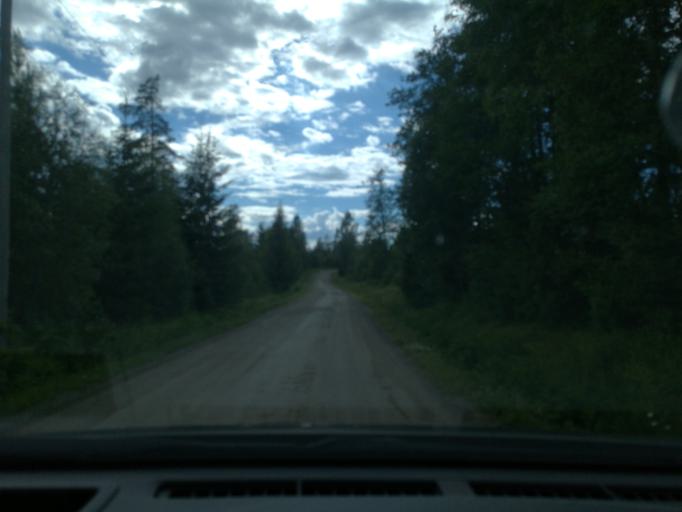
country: SE
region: Vaestmanland
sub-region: Surahammars Kommun
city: Ramnas
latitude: 59.8208
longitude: 16.2660
